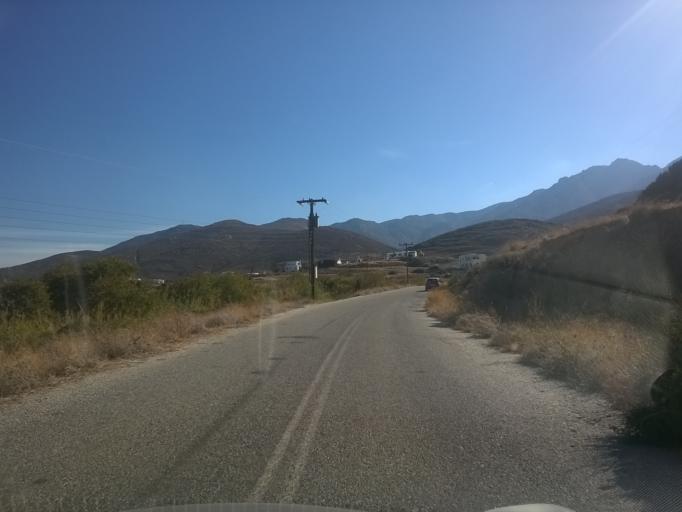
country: GR
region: South Aegean
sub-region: Nomos Kykladon
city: Naxos
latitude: 37.1401
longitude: 25.4537
